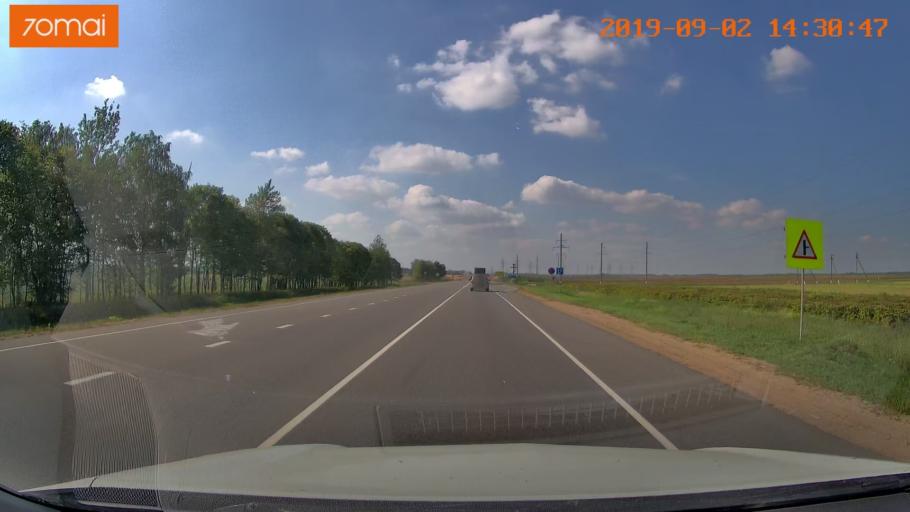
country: BY
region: Mogilev
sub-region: Mahilyowski Rayon
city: Kadino
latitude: 53.8633
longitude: 30.4972
